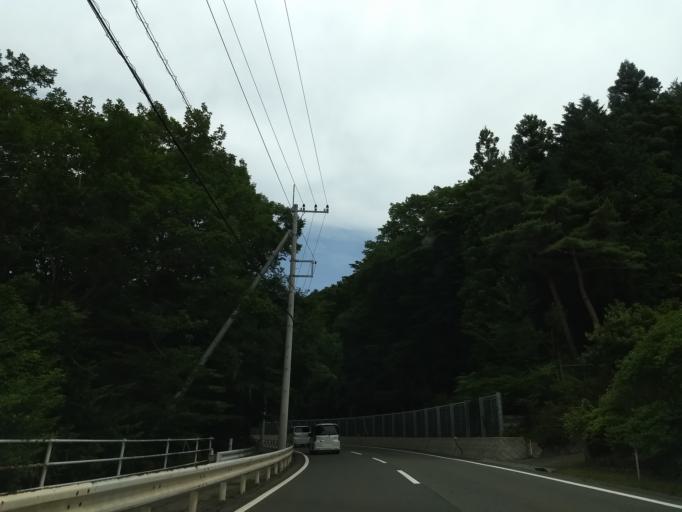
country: JP
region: Shizuoka
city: Gotemba
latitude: 35.3733
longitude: 138.8601
